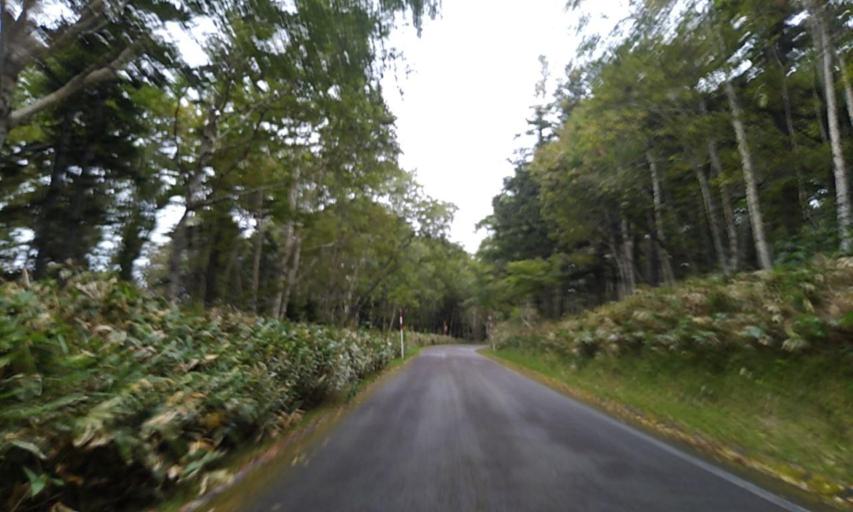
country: JP
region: Hokkaido
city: Bihoro
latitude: 43.5691
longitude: 144.2211
